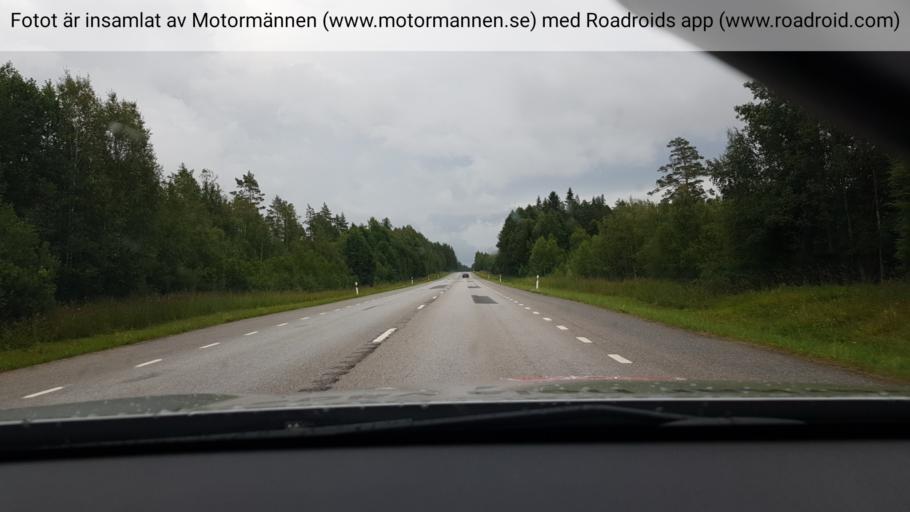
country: SE
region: Uppsala
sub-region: Alvkarleby Kommun
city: AElvkarleby
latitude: 60.5502
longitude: 17.5061
